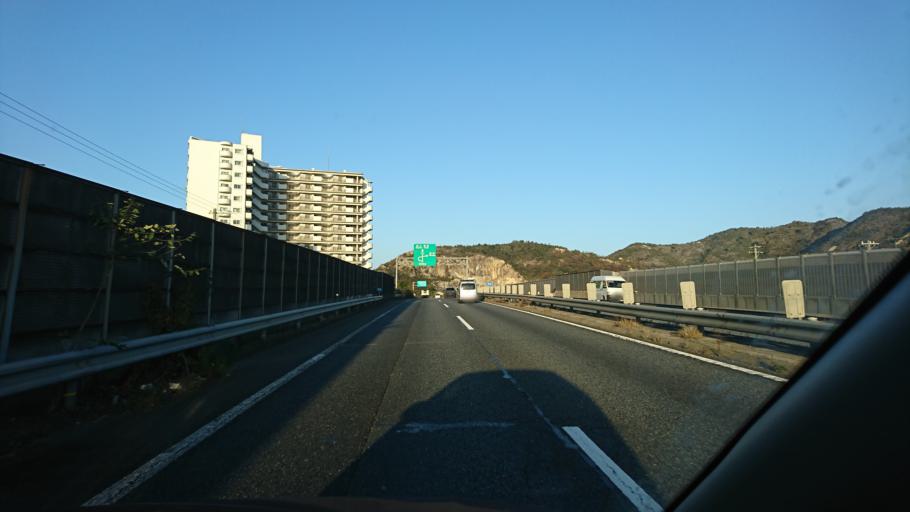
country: JP
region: Hyogo
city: Kakogawacho-honmachi
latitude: 34.7910
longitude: 134.8070
